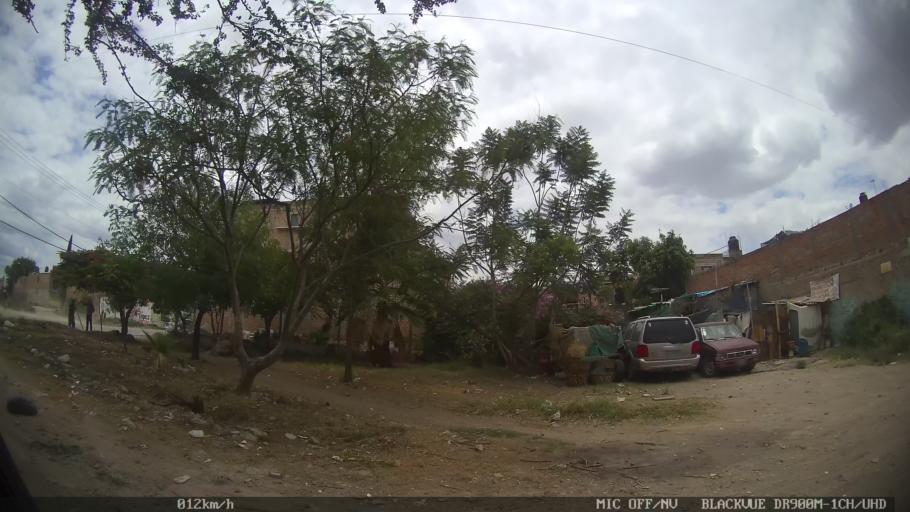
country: MX
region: Jalisco
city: Tlaquepaque
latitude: 20.6520
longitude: -103.2657
